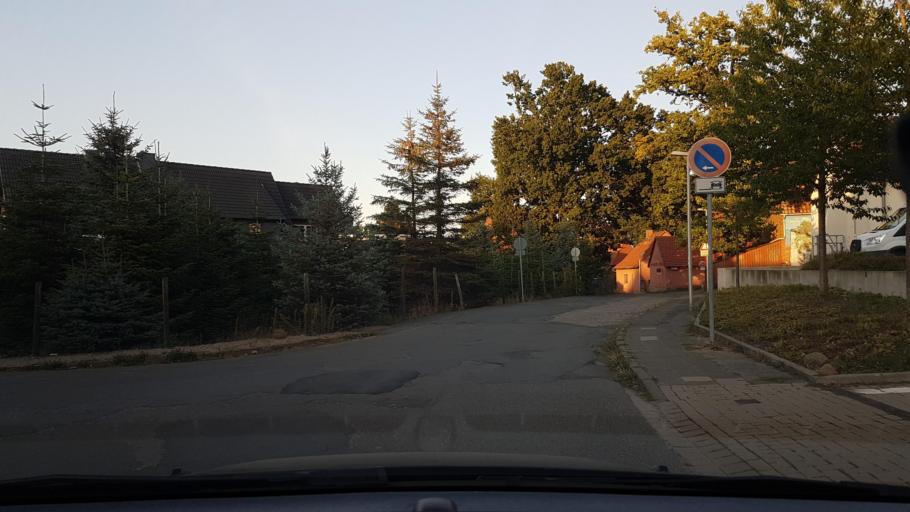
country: DE
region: Lower Saxony
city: Elze
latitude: 52.5445
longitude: 9.7312
